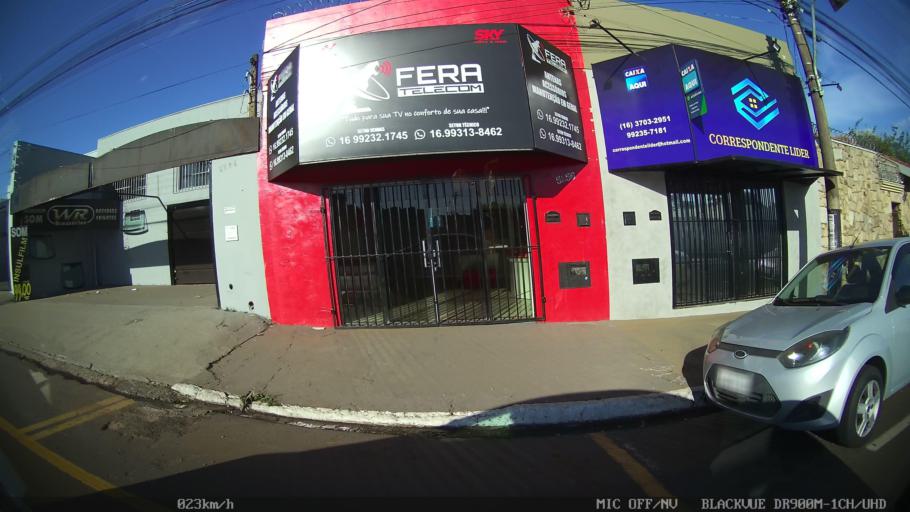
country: BR
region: Sao Paulo
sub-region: Franca
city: Franca
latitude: -20.5082
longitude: -47.3992
